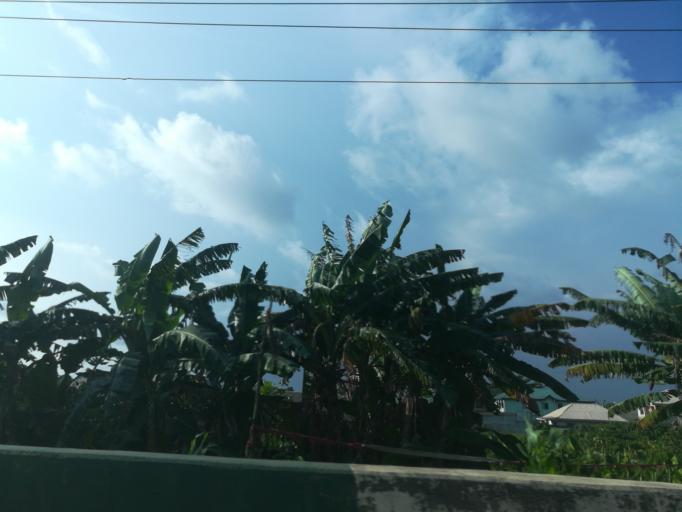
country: NG
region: Ogun
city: Ado Odo
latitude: 6.4872
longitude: 3.0672
